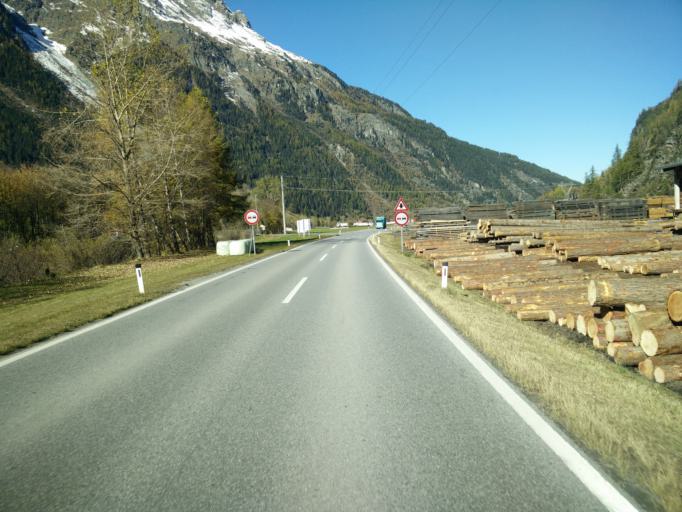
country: AT
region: Tyrol
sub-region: Politischer Bezirk Imst
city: Soelden
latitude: 47.0447
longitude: 10.9708
